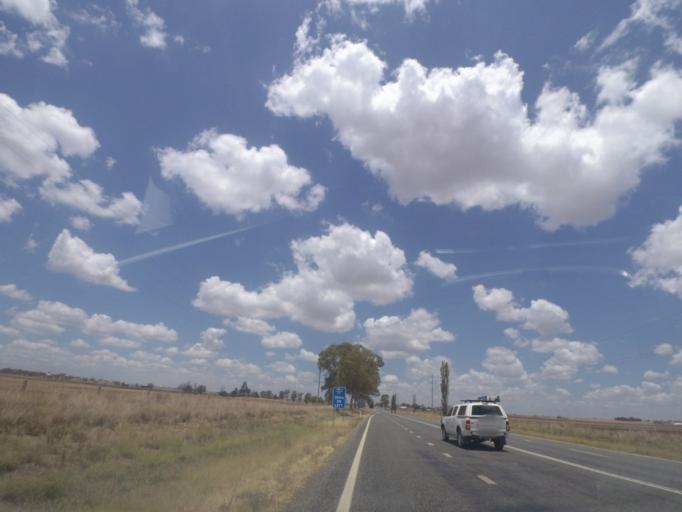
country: AU
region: Queensland
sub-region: Toowoomba
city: Top Camp
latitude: -27.9232
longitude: 151.9836
